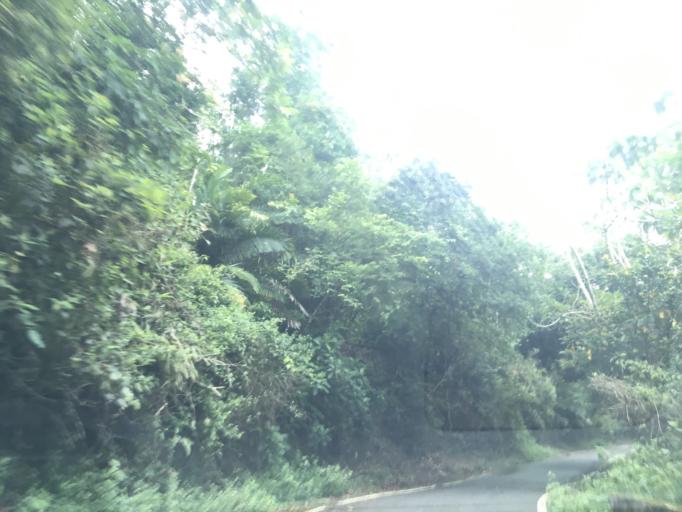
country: TW
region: Taiwan
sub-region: Yunlin
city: Douliu
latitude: 23.5697
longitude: 120.6365
